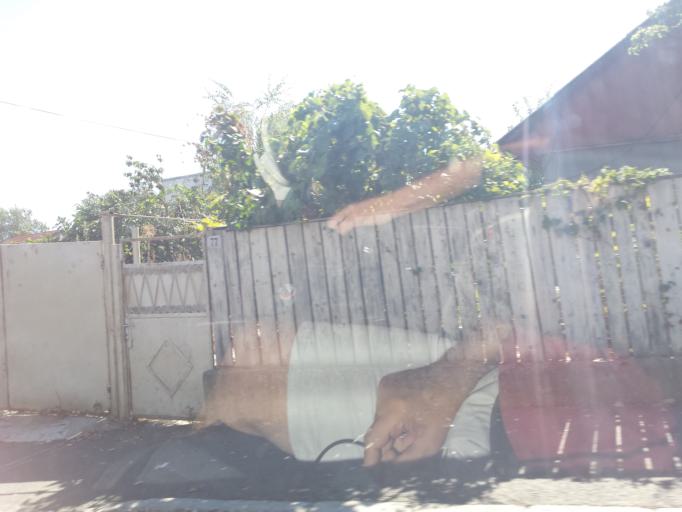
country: RO
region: Tulcea
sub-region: Municipiul Tulcea
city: Tulcea
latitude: 45.1699
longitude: 28.7927
